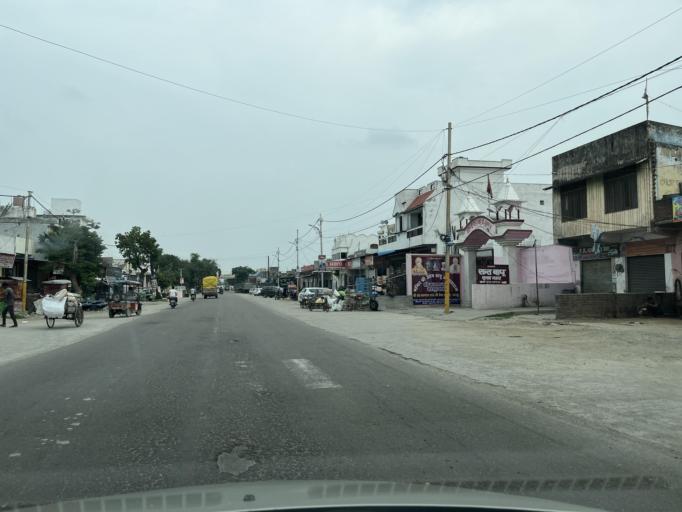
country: IN
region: Uttar Pradesh
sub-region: Rampur
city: Bilaspur
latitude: 29.0386
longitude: 79.2527
